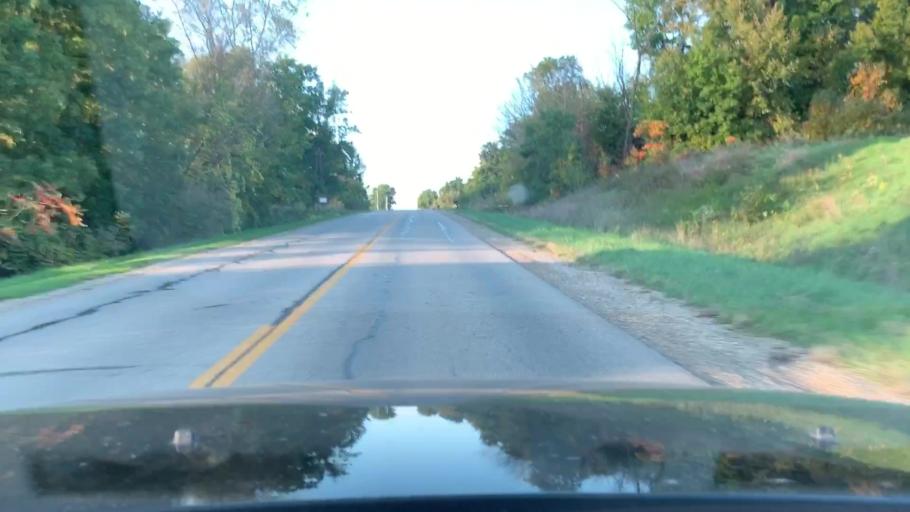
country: US
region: Michigan
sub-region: Ottawa County
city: Hudsonville
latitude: 42.7985
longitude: -85.8418
